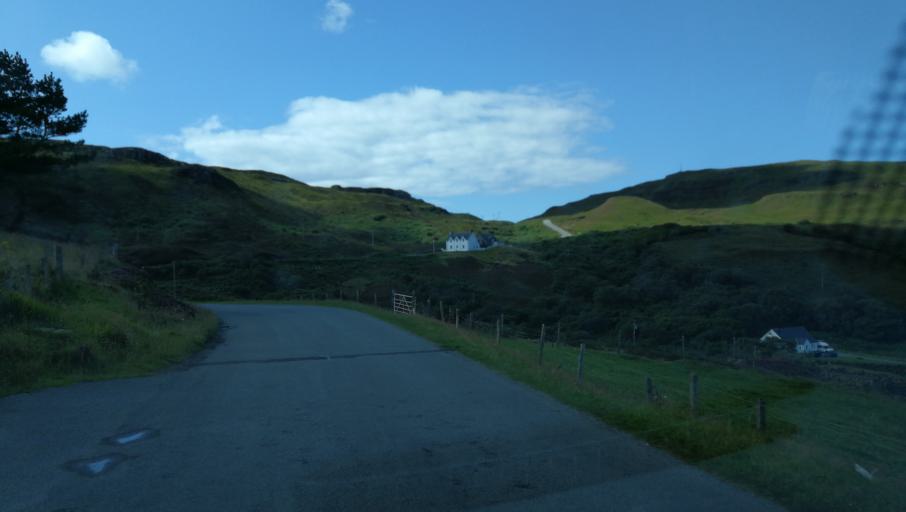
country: GB
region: Scotland
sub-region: Highland
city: Isle of Skye
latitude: 57.4524
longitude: -6.6623
